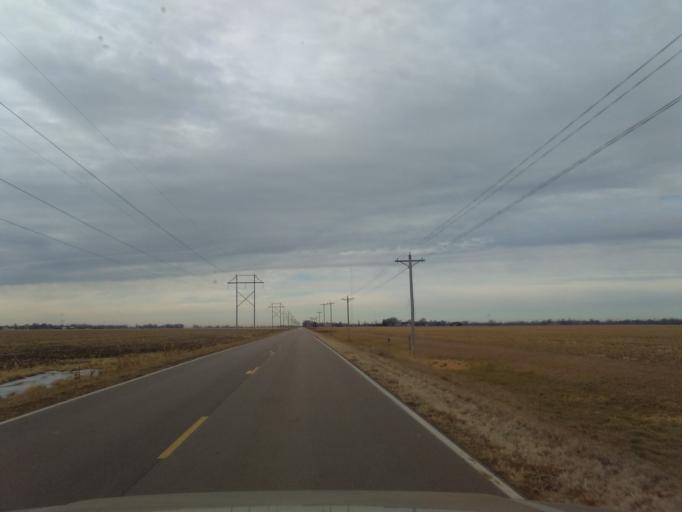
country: US
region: Nebraska
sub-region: Buffalo County
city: Gibbon
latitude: 40.6550
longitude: -98.8213
